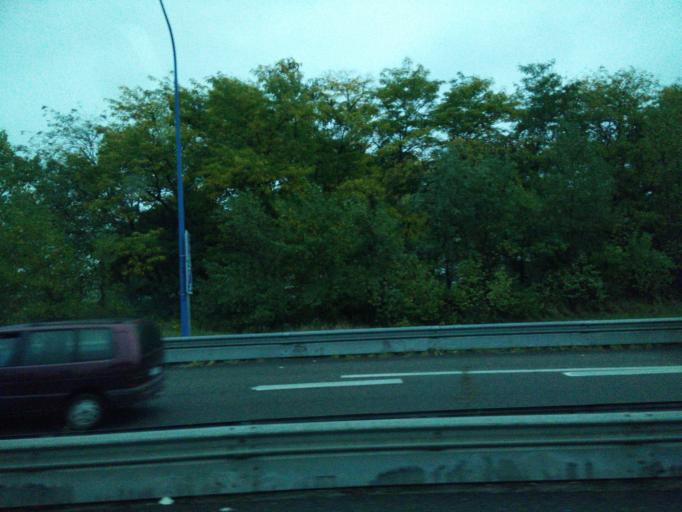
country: FR
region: Midi-Pyrenees
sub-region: Departement de la Haute-Garonne
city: Blagnac
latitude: 43.6223
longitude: 1.4191
